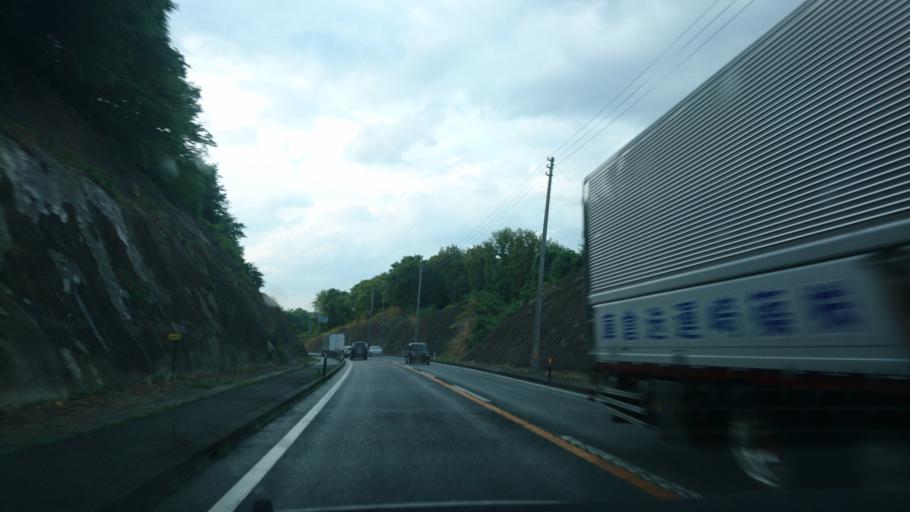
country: JP
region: Iwate
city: Ichinoseki
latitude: 38.9564
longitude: 141.1226
